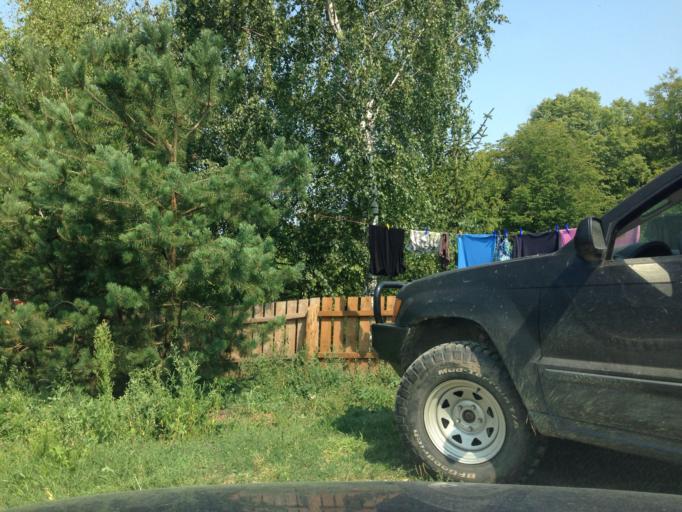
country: PL
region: Kujawsko-Pomorskie
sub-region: Powiat golubsko-dobrzynski
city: Golub-Dobrzyn
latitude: 53.0618
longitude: 19.0288
